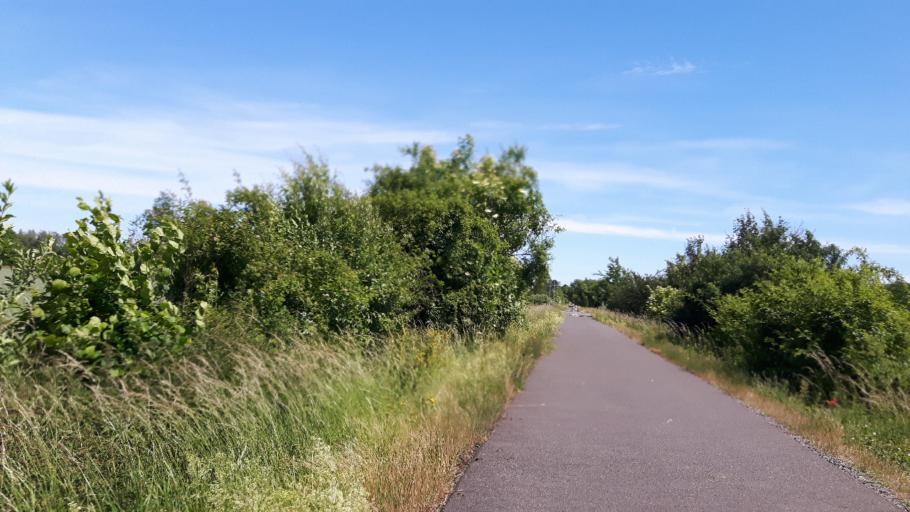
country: DE
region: Saxony
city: Kitzen
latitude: 51.2586
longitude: 12.2058
